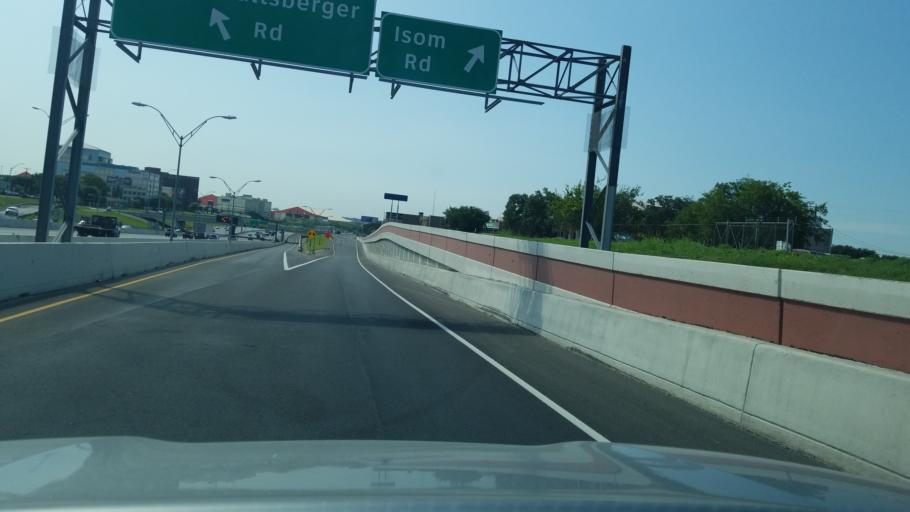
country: US
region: Texas
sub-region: Bexar County
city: Castle Hills
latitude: 29.5353
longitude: -98.4909
